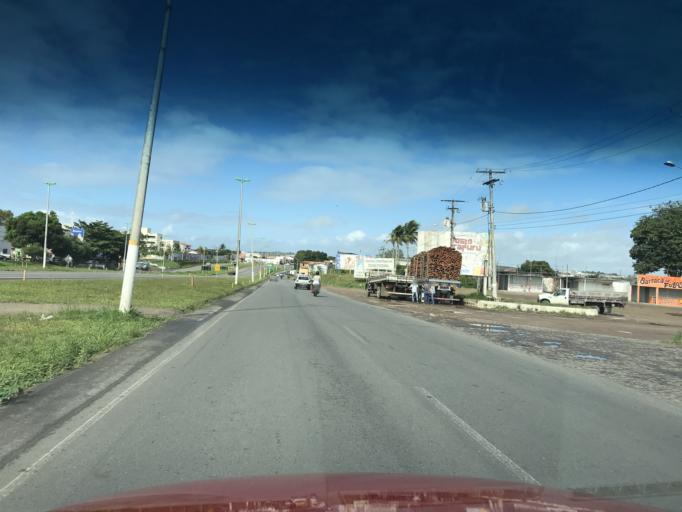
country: BR
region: Bahia
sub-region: Santo Antonio De Jesus
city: Santo Antonio de Jesus
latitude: -12.9659
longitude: -39.2727
